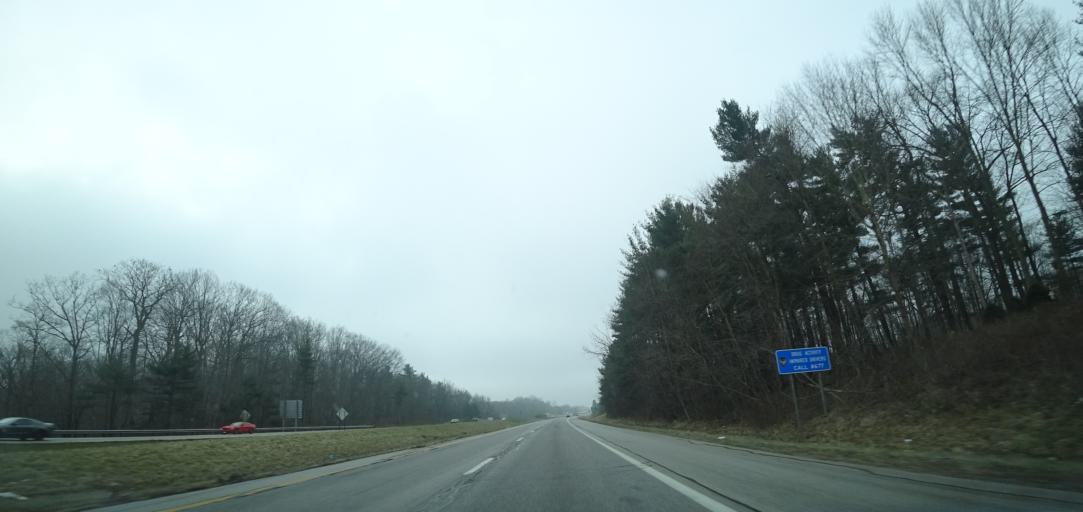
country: US
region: Ohio
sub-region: Summit County
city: Richfield
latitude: 41.2524
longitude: -81.6304
